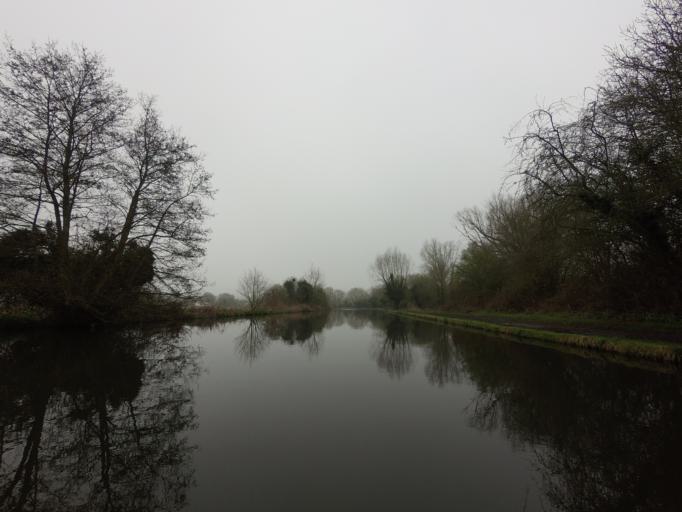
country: GB
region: England
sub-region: Hertfordshire
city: Bovingdon
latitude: 51.7493
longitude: -0.5281
